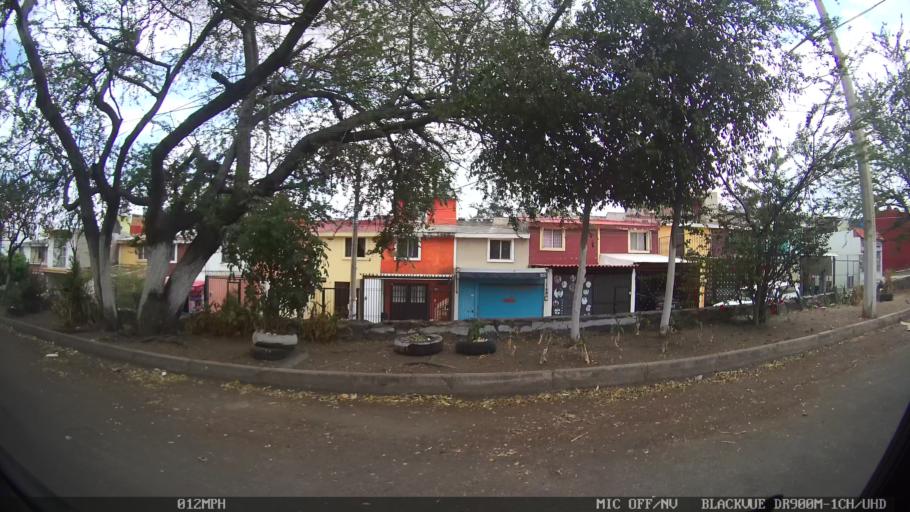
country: MX
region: Jalisco
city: Tonala
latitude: 20.6310
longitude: -103.2584
